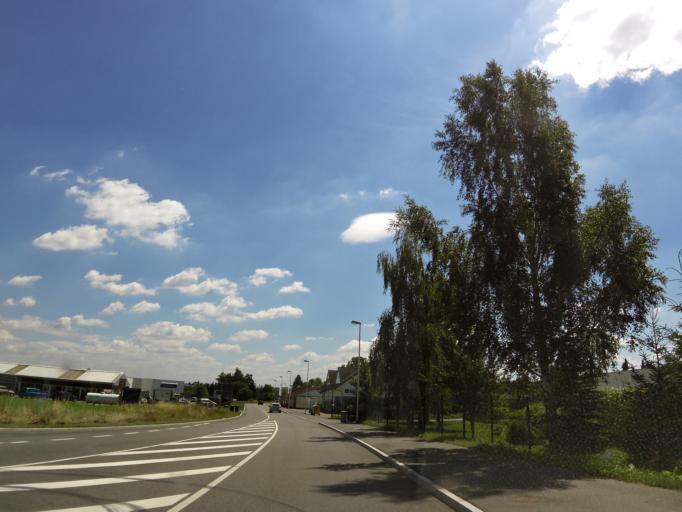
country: DE
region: Saxony
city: Pfaffroda
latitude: 50.8339
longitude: 12.5185
